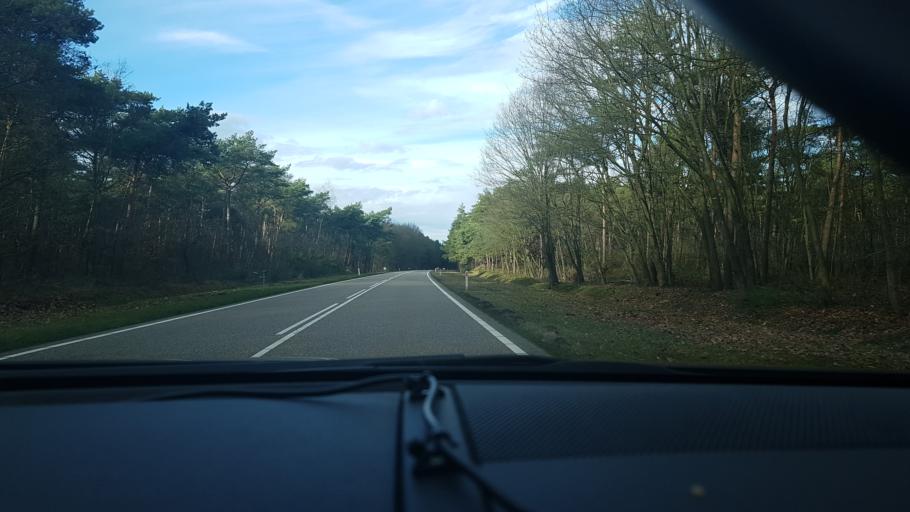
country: NL
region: Limburg
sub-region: Gemeente Peel en Maas
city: Maasbree
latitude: 51.3164
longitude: 6.0485
